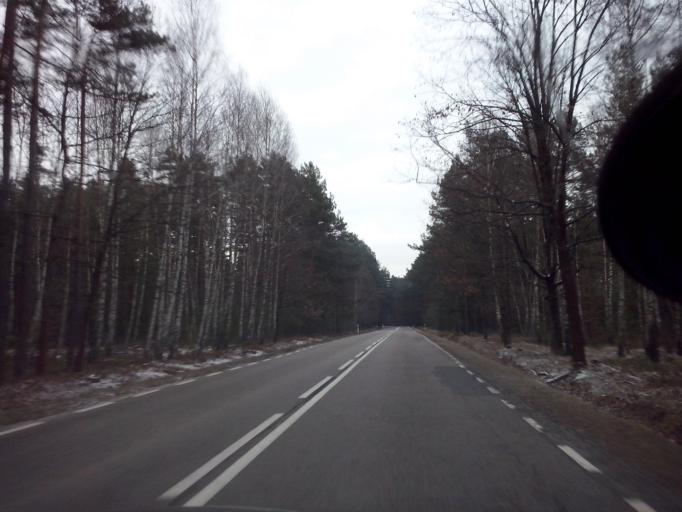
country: PL
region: Lublin Voivodeship
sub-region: Powiat bilgorajski
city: Biszcza
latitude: 50.5035
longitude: 22.5918
